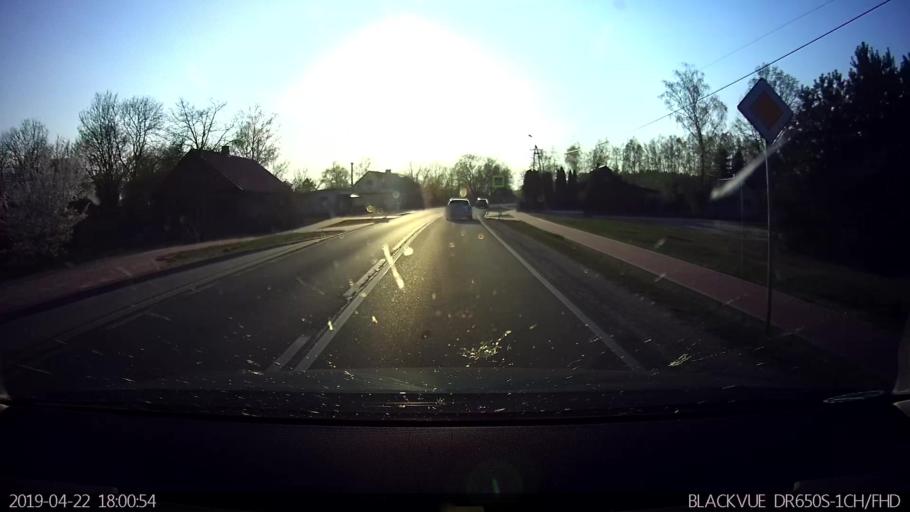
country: PL
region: Masovian Voivodeship
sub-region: Powiat wegrowski
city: Korytnica
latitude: 52.4768
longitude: 21.8390
